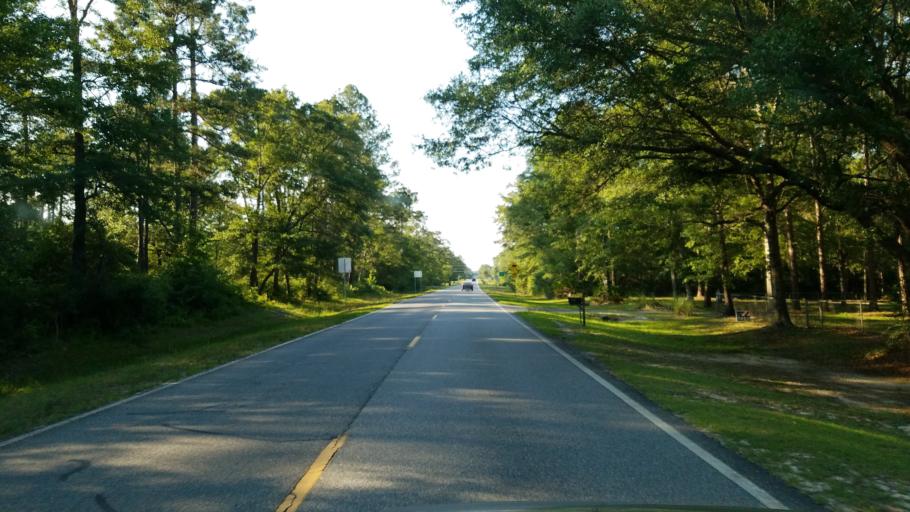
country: US
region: Georgia
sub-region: Lanier County
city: Lakeland
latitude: 30.9466
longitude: -83.0816
